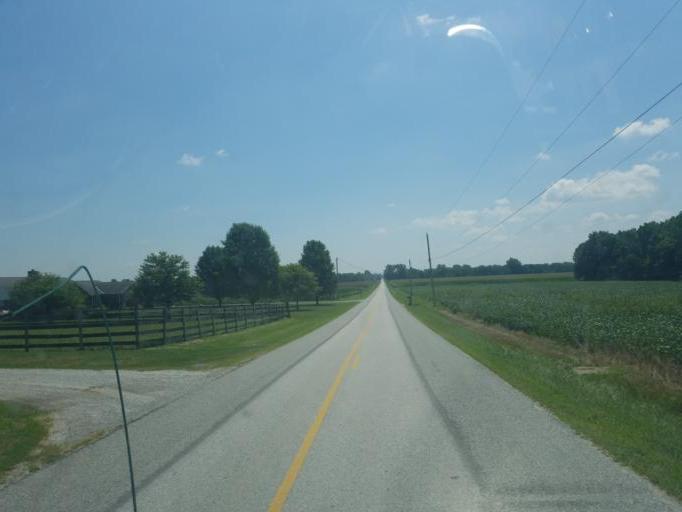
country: US
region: Ohio
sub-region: Auglaize County
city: Saint Marys
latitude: 40.5535
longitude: -84.2974
